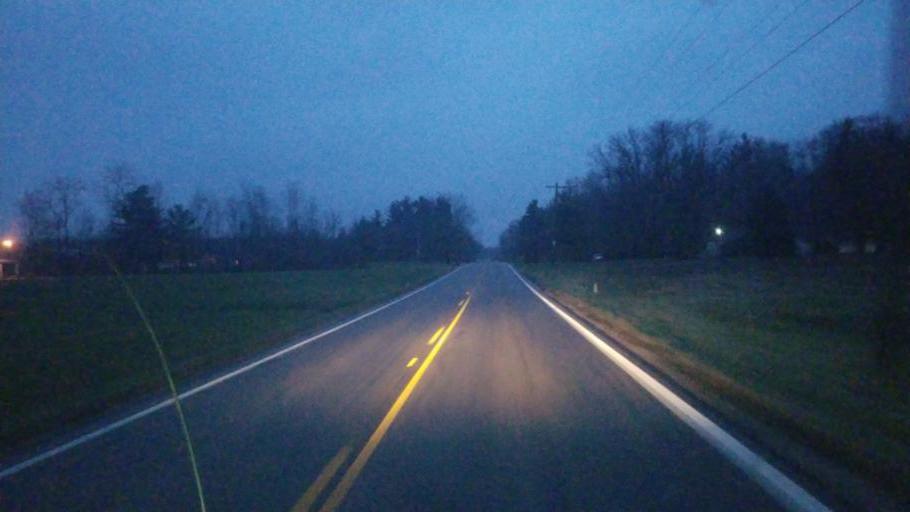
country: US
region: Ohio
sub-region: Morrow County
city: Mount Gilead
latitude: 40.5099
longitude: -82.8175
